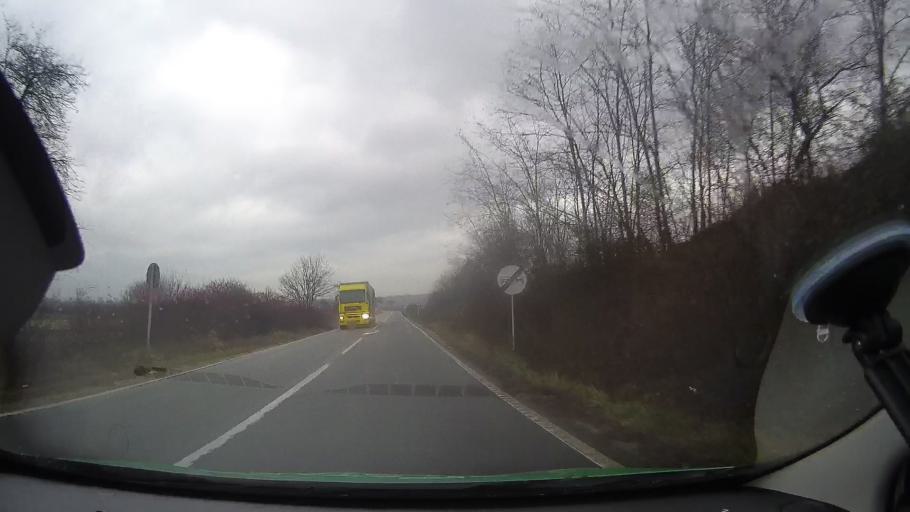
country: RO
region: Arad
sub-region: Comuna Almas
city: Almas
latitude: 46.2951
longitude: 22.2061
